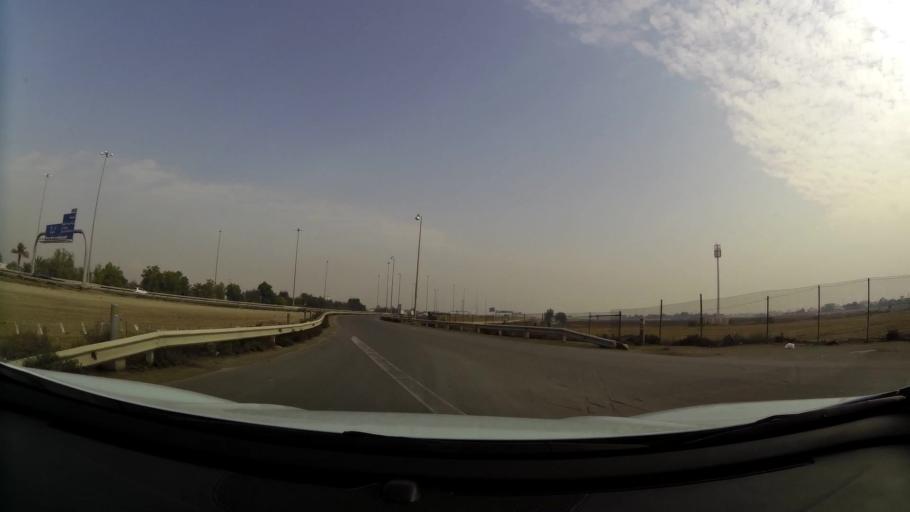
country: AE
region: Abu Dhabi
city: Abu Dhabi
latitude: 24.6713
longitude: 54.7631
